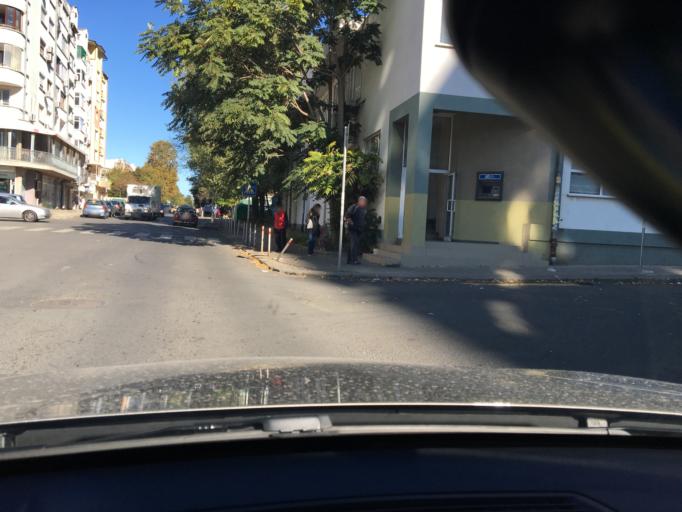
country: BG
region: Burgas
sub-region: Obshtina Burgas
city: Burgas
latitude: 42.5208
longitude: 27.4511
